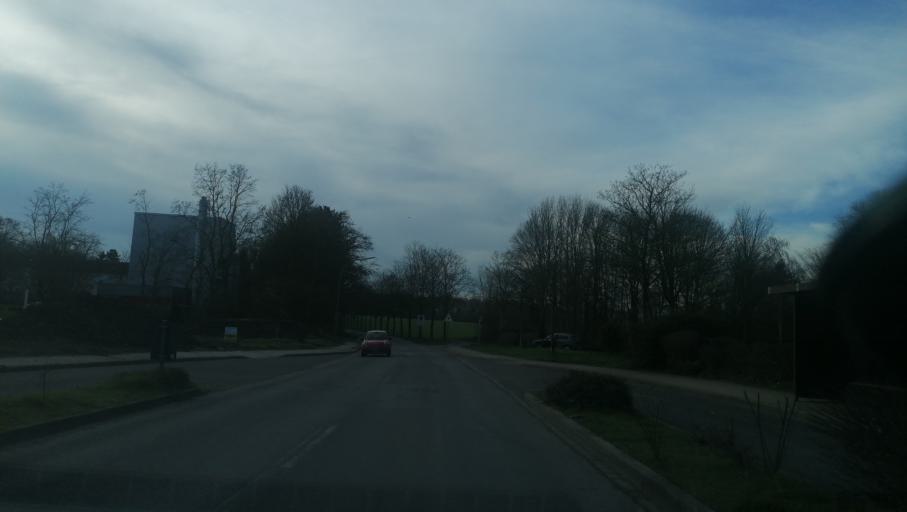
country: DE
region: North Rhine-Westphalia
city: Bergkamen
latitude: 51.6061
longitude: 7.6094
